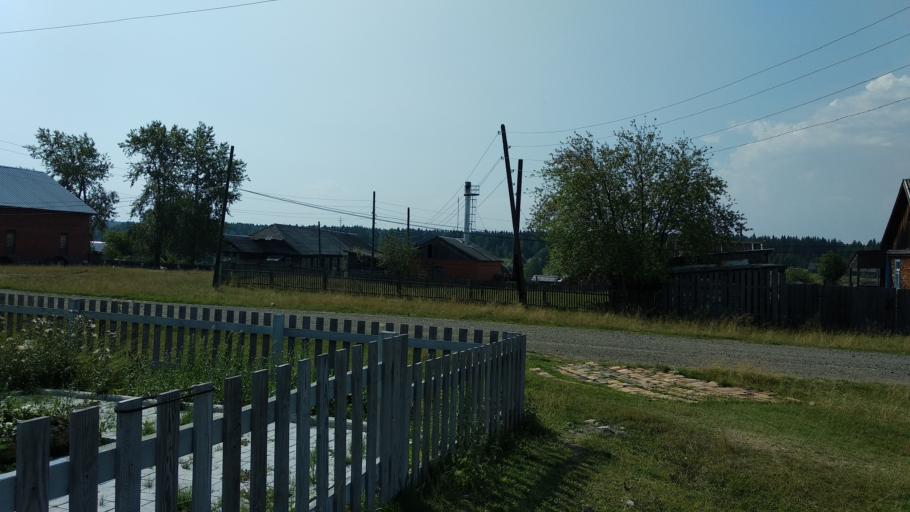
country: RU
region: Sverdlovsk
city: Karpinsk
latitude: 59.4484
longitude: 60.0133
